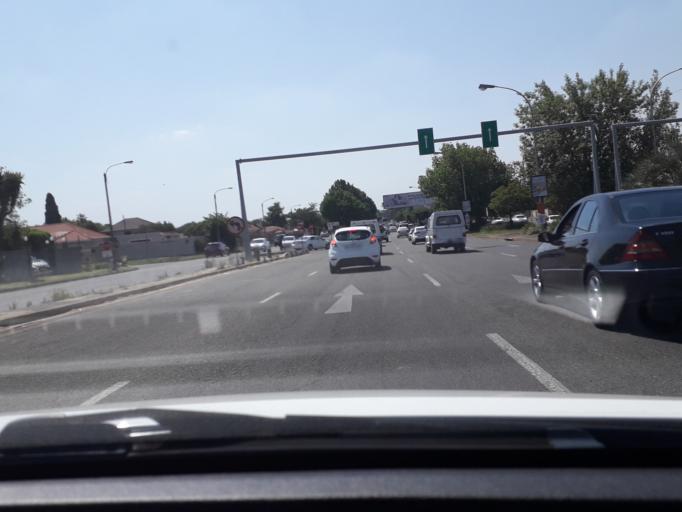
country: ZA
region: Gauteng
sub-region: City of Johannesburg Metropolitan Municipality
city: Modderfontein
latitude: -26.1557
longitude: 28.1627
